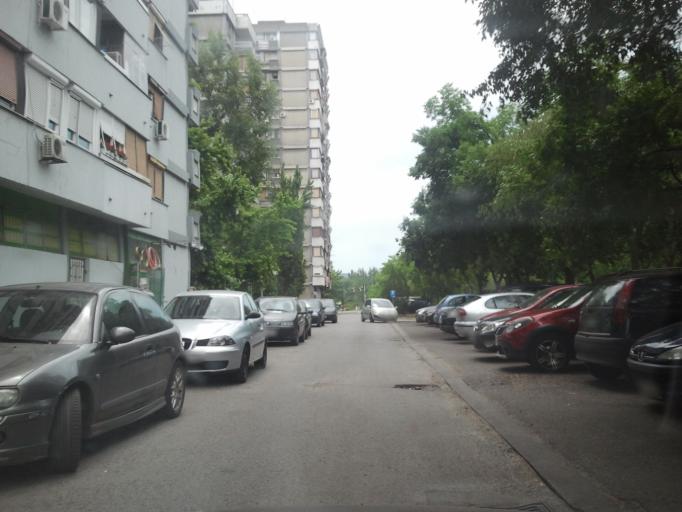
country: RS
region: Autonomna Pokrajina Vojvodina
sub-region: Juznobacki Okrug
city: Novi Sad
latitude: 45.2417
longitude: 19.8373
